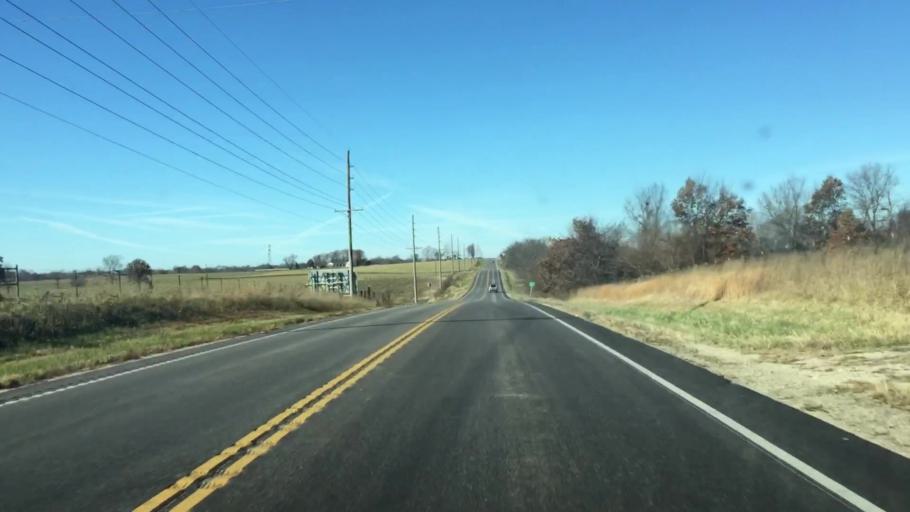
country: US
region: Missouri
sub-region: Miller County
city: Eldon
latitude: 38.3737
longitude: -92.6316
